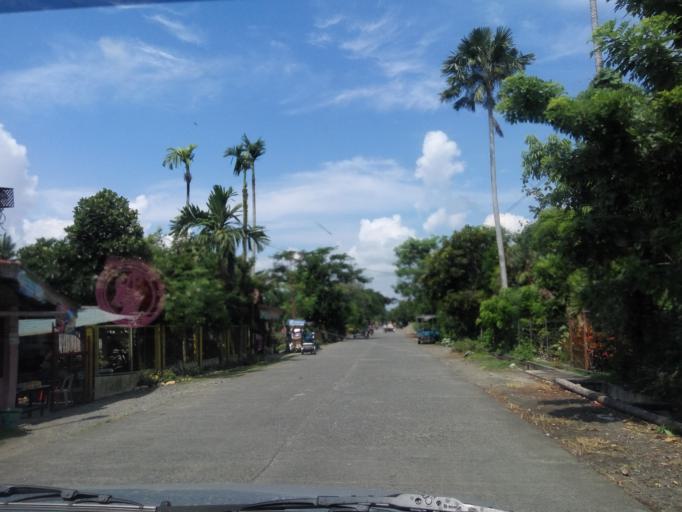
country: PH
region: Central Luzon
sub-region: Province of Aurora
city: Maria Aurora
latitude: 15.8250
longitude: 121.5128
